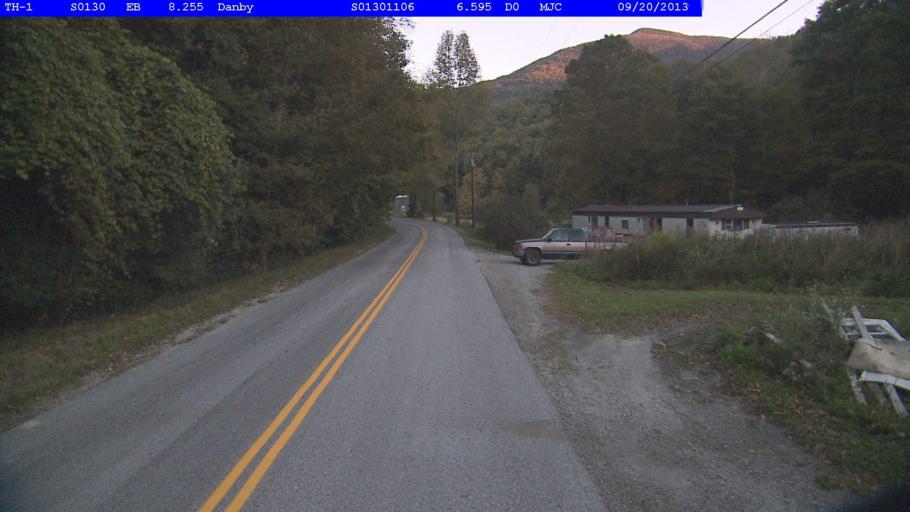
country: US
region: Vermont
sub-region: Bennington County
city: Manchester Center
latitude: 43.3409
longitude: -73.0234
